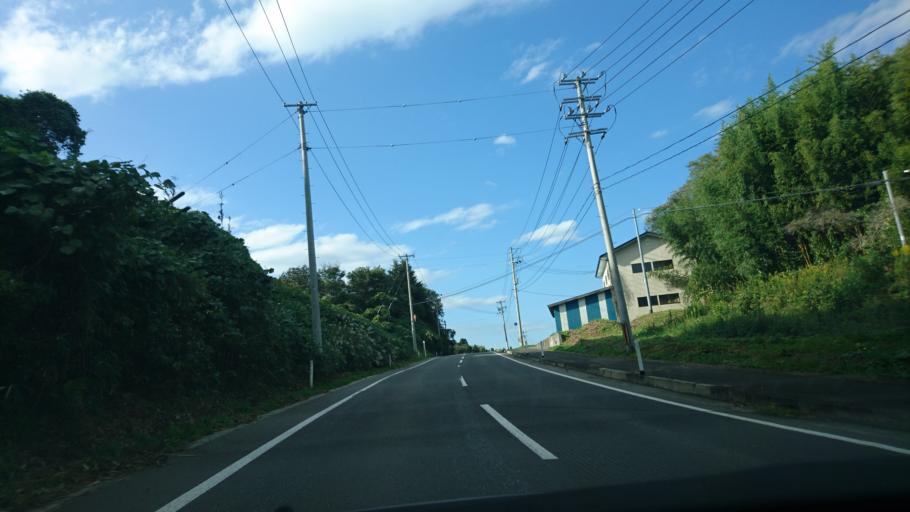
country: JP
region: Iwate
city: Ichinoseki
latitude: 38.8786
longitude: 141.3339
